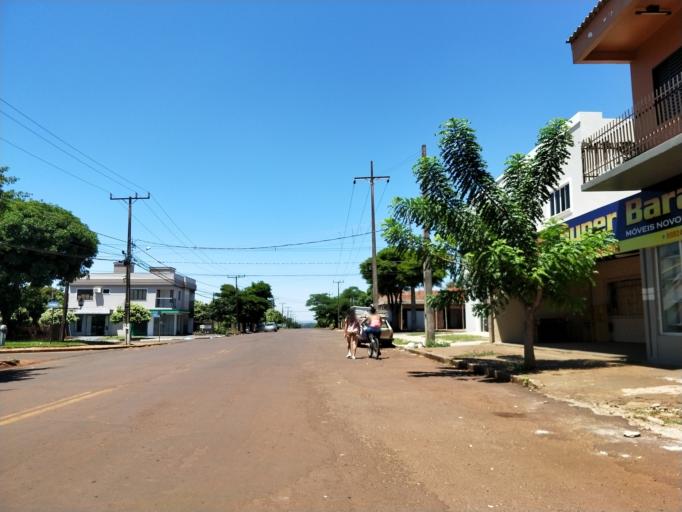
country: BR
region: Parana
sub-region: Marechal Candido Rondon
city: Marechal Candido Rondon
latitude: -24.5661
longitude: -54.0587
